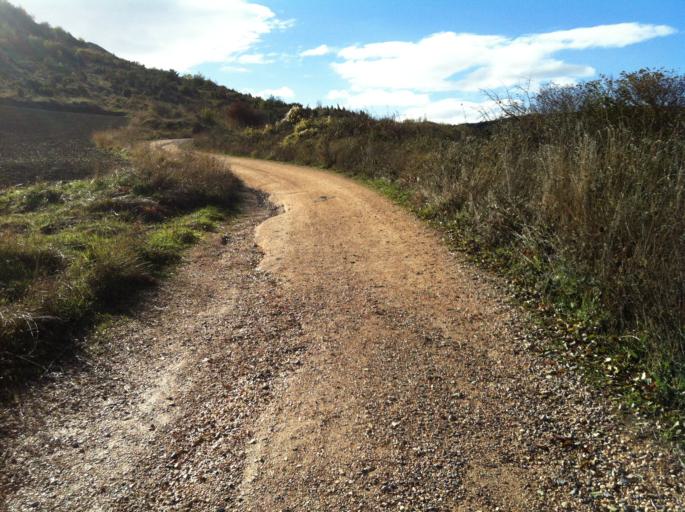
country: ES
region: Basque Country
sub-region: Provincia de Alava
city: Gasteiz / Vitoria
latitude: 42.8198
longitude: -2.6647
